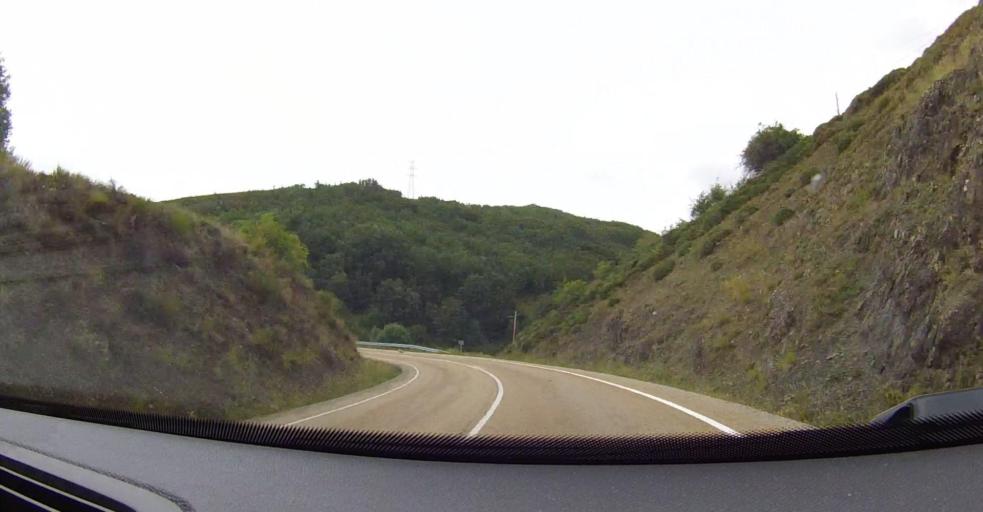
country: ES
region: Castille and Leon
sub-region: Provincia de Leon
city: Puebla de Lillo
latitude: 42.9333
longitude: -5.2731
